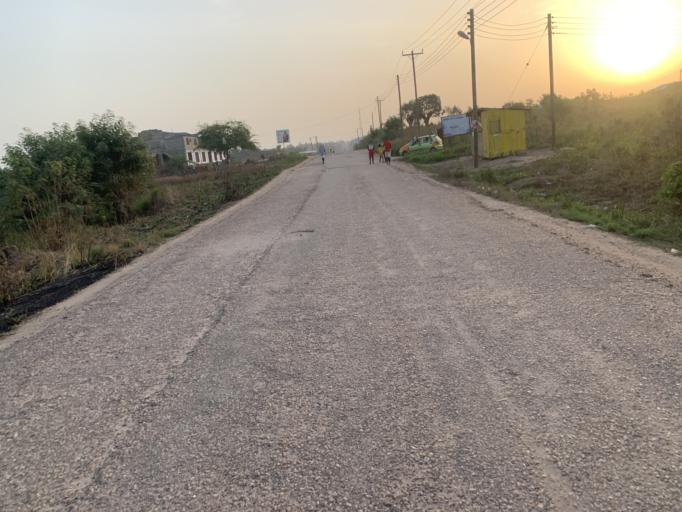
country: GH
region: Central
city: Winneba
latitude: 5.3586
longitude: -0.6069
